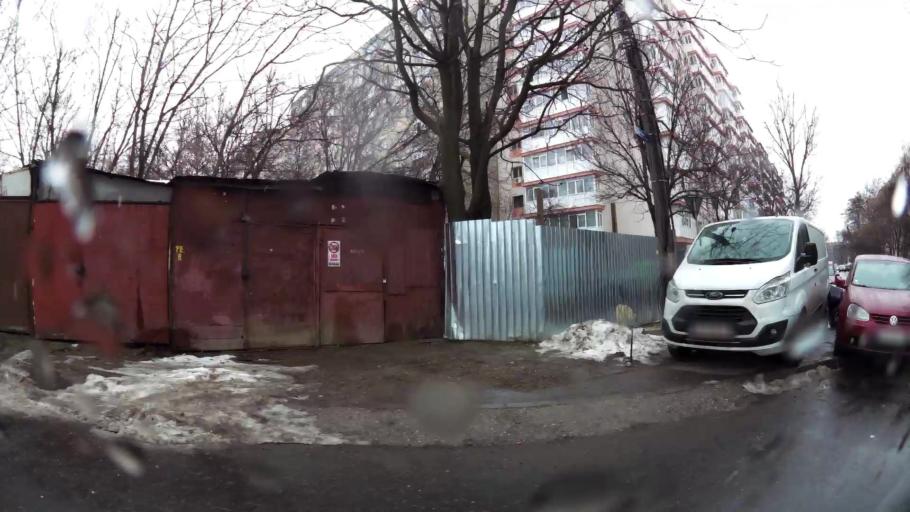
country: RO
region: Ilfov
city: Dobroesti
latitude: 44.4178
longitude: 26.1821
